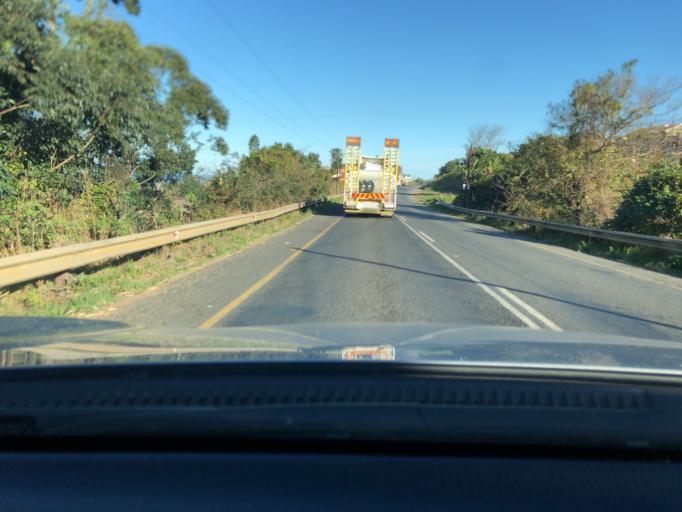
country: ZA
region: KwaZulu-Natal
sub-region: eThekwini Metropolitan Municipality
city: Umkomaas
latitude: -30.0147
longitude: 30.8074
